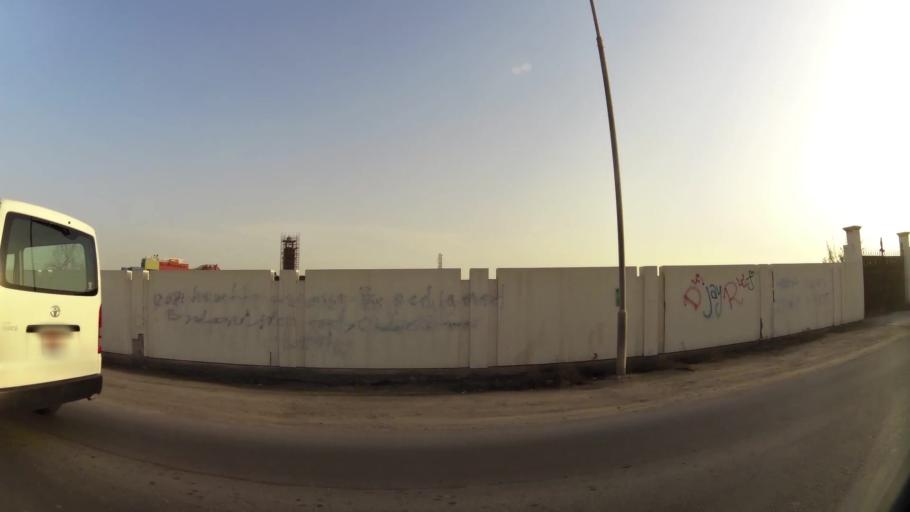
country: BH
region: Manama
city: Jidd Hafs
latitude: 26.2020
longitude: 50.4966
